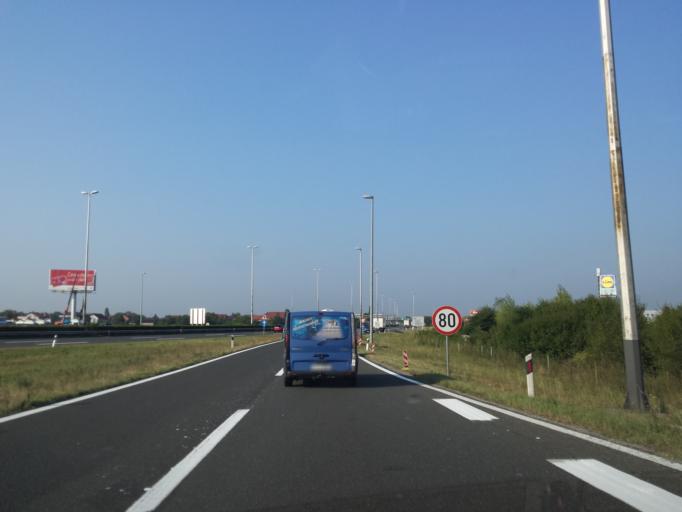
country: HR
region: Grad Zagreb
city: Lucko
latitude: 45.7562
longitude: 15.8924
